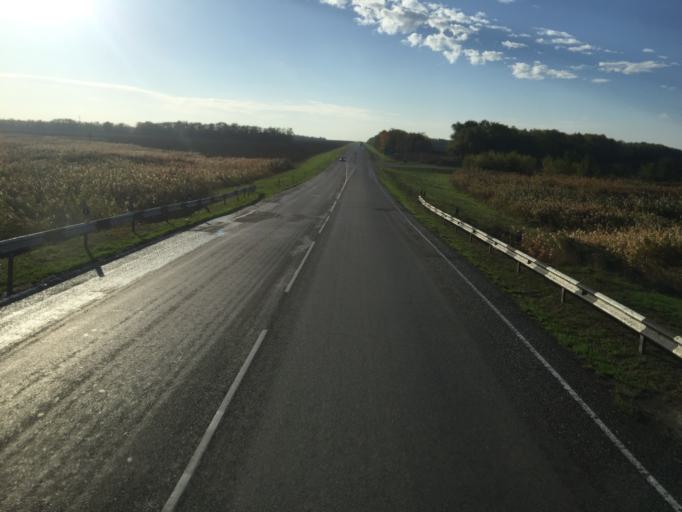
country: RU
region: Rostov
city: Mechetinskaya
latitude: 46.7155
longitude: 40.4919
